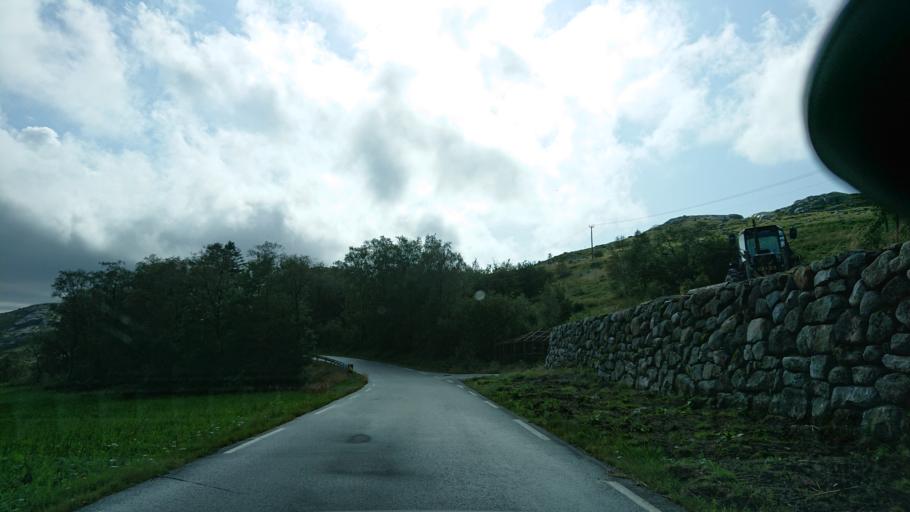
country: NO
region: Rogaland
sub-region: Gjesdal
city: Algard
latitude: 58.6932
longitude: 5.8814
